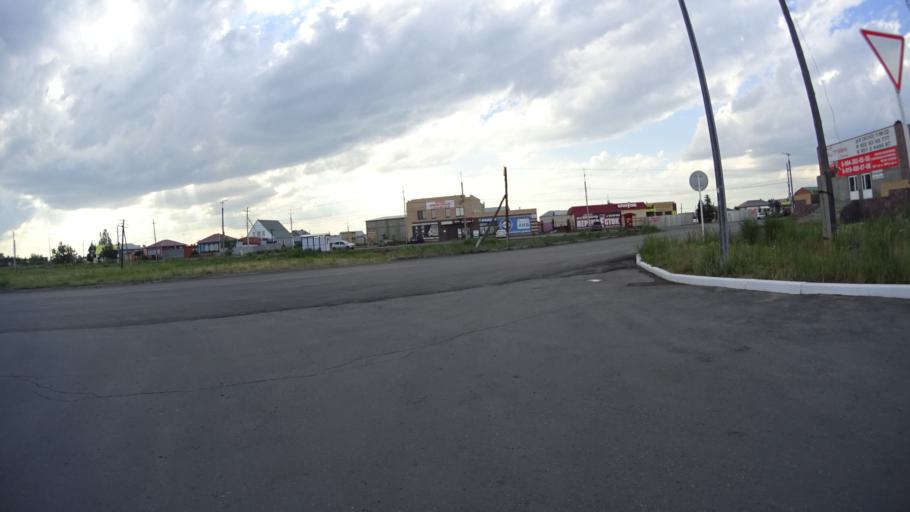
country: RU
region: Chelyabinsk
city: Troitsk
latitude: 54.0828
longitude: 61.5188
